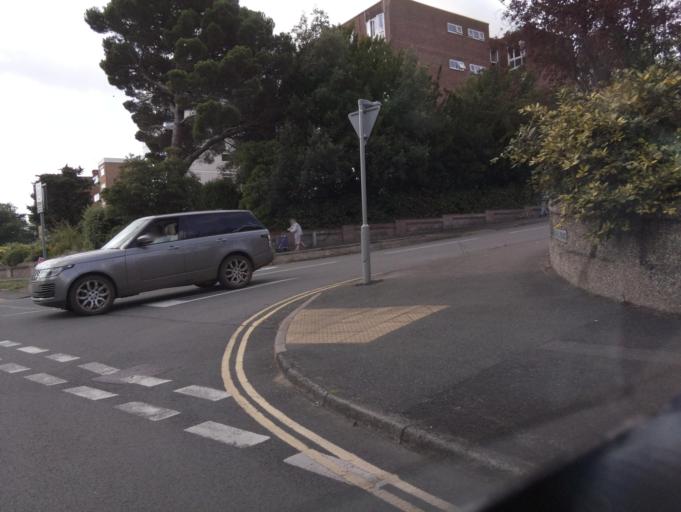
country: GB
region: England
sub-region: Dorset
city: Parkstone
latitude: 50.7213
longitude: -1.9672
